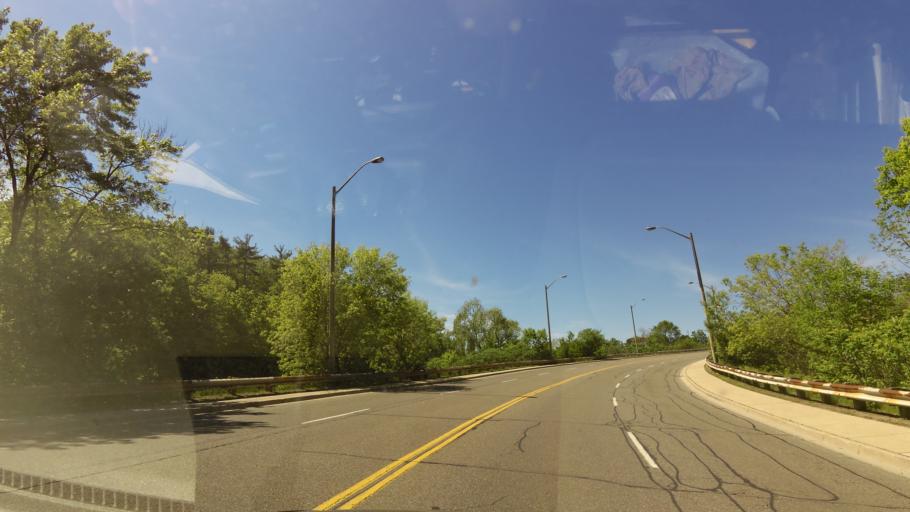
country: CA
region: Ontario
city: Oakville
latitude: 43.4511
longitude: -79.6867
